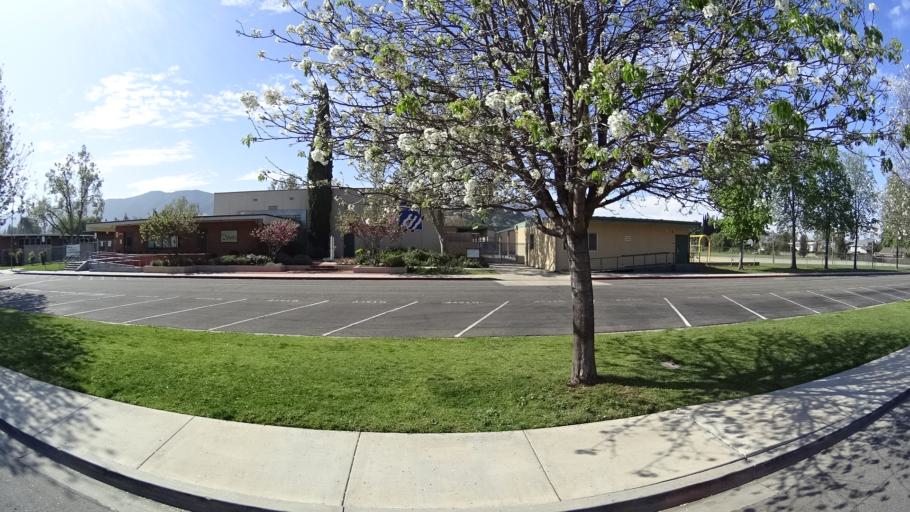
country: US
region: California
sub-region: Ventura County
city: Casa Conejo
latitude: 34.1831
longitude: -118.9328
